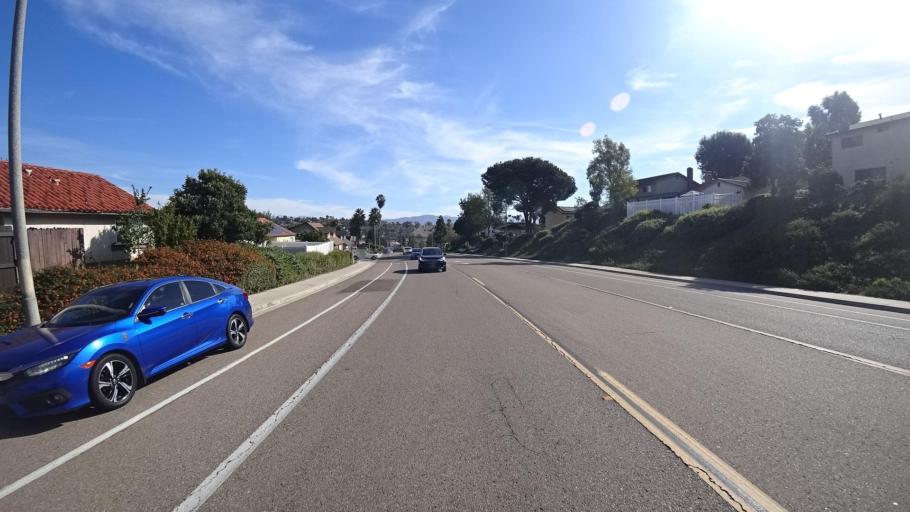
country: US
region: California
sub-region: San Diego County
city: Spring Valley
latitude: 32.7311
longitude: -116.9807
